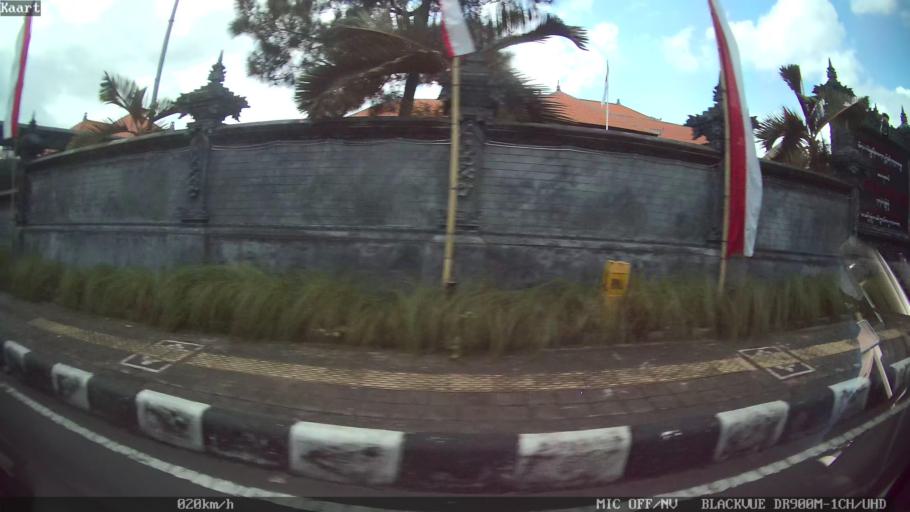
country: ID
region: Bali
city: Klungkung
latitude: -8.5347
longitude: 115.3996
